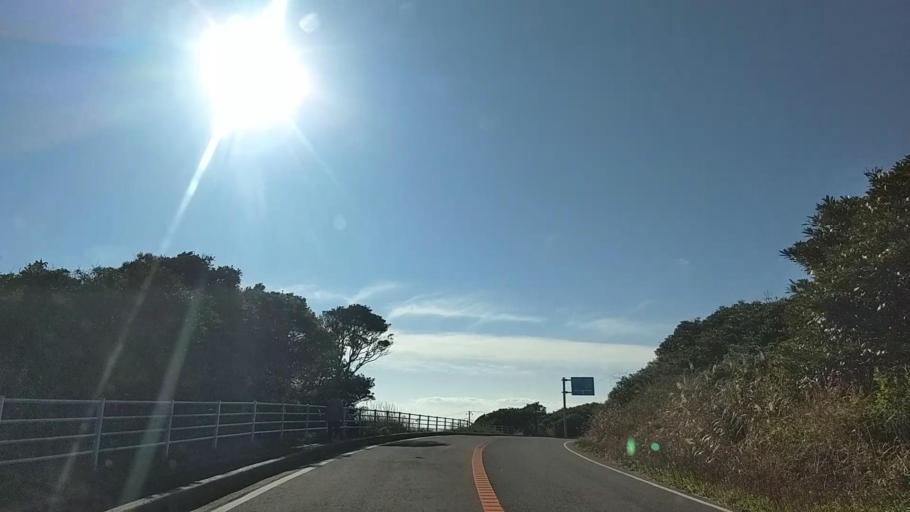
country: JP
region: Chiba
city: Hasaki
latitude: 35.6985
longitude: 140.8618
